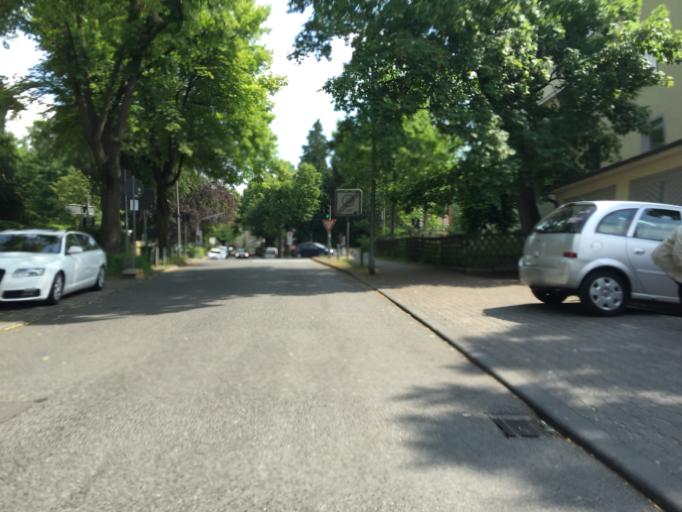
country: DE
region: Hesse
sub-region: Regierungsbezirk Darmstadt
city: Wiesbaden
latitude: 50.0741
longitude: 8.2536
